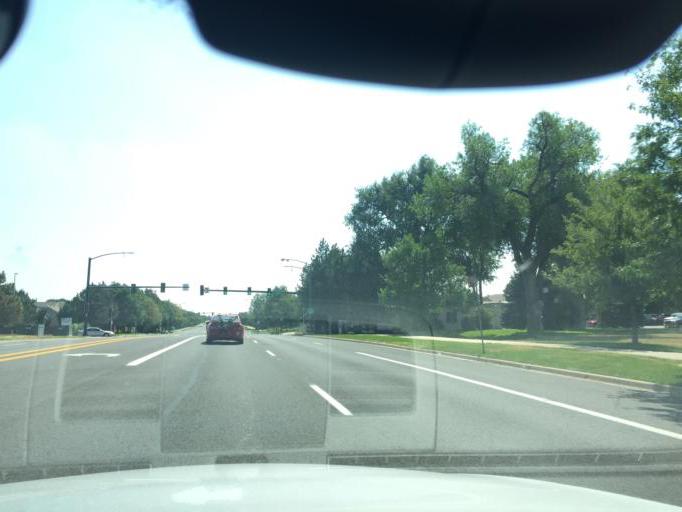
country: US
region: Colorado
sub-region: Adams County
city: Northglenn
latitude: 39.8996
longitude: -105.0353
